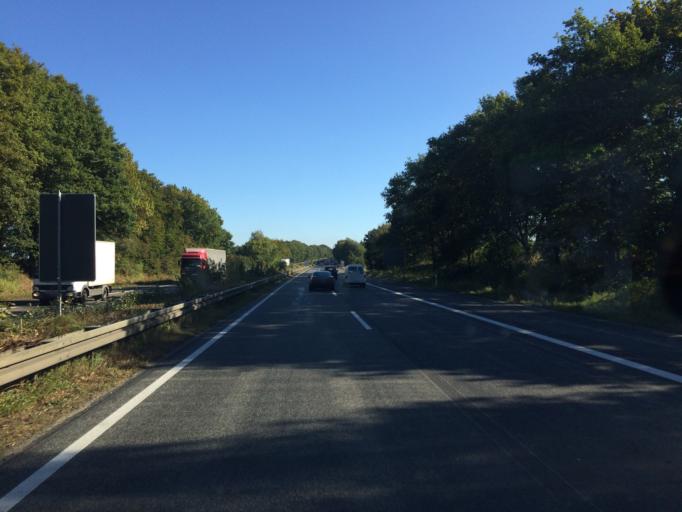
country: DE
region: Saarland
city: Bexbach
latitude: 49.3309
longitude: 7.2806
